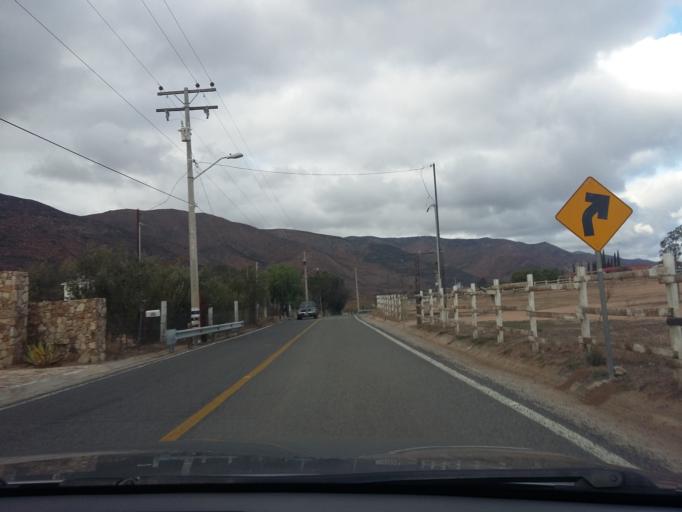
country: MX
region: Baja California
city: El Sauzal
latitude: 32.0255
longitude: -116.6740
